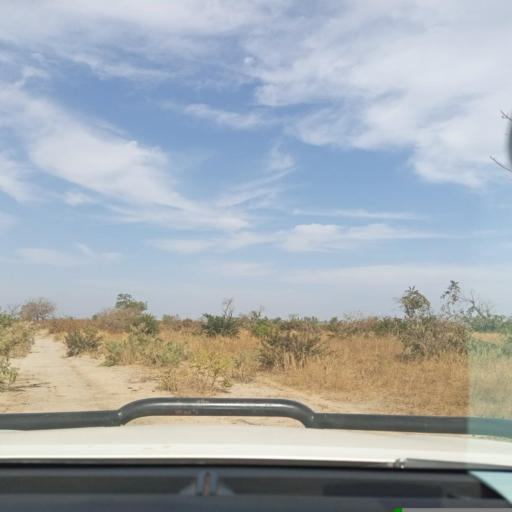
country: ML
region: Koulikoro
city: Kati
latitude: 12.7507
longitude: -8.2497
